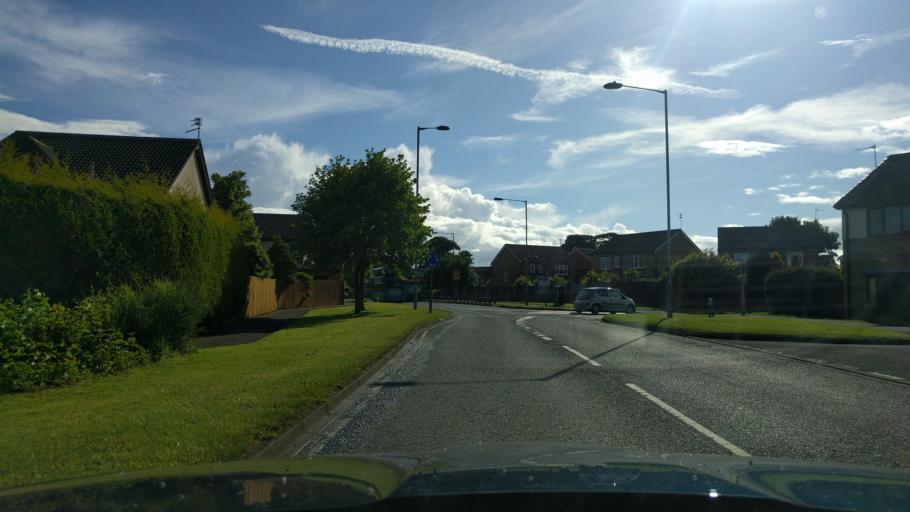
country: GB
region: England
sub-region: Northumberland
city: Cramlington
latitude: 55.0993
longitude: -1.5870
